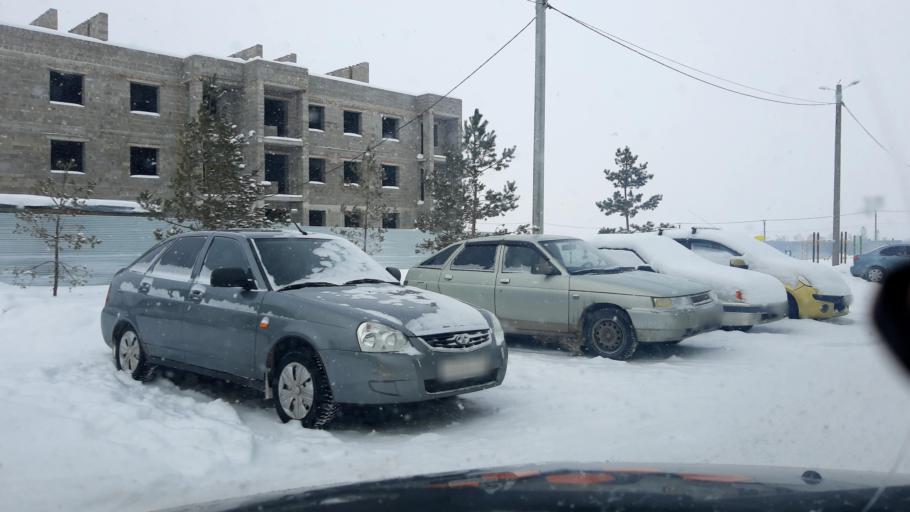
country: RU
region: Bashkortostan
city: Avdon
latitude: 54.4846
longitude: 55.8857
